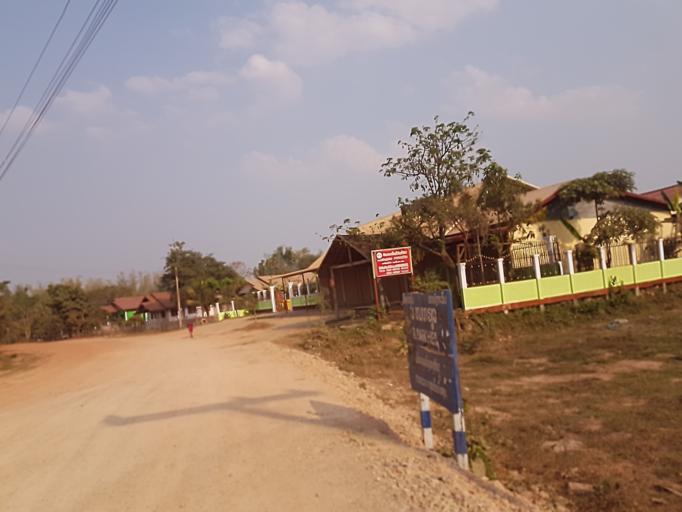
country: TH
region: Nong Khai
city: Phon Phisai
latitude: 18.0001
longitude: 102.9090
